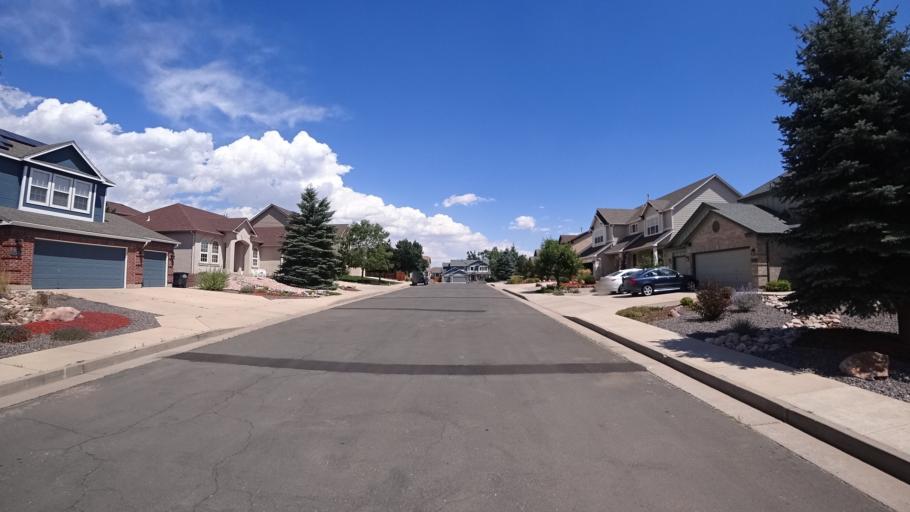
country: US
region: Colorado
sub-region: El Paso County
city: Black Forest
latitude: 38.9553
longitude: -104.7605
